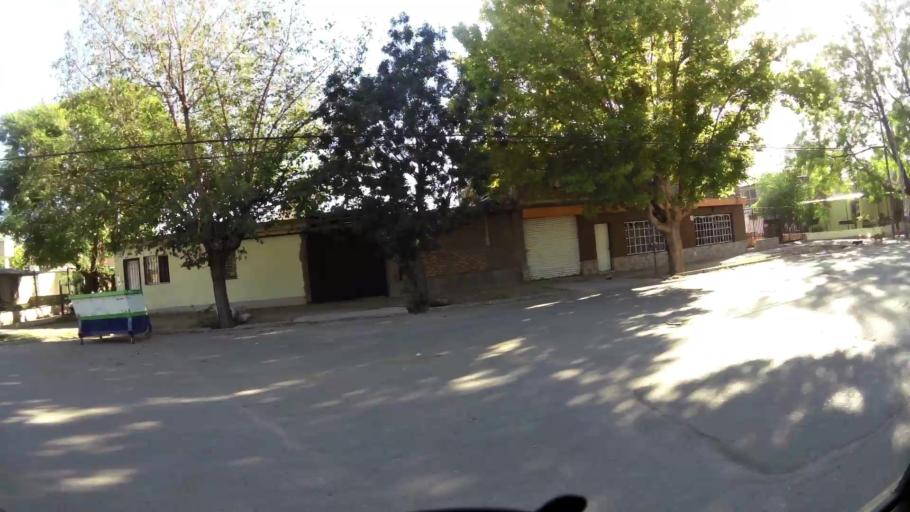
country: AR
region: Mendoza
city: Las Heras
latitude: -32.8563
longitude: -68.8159
